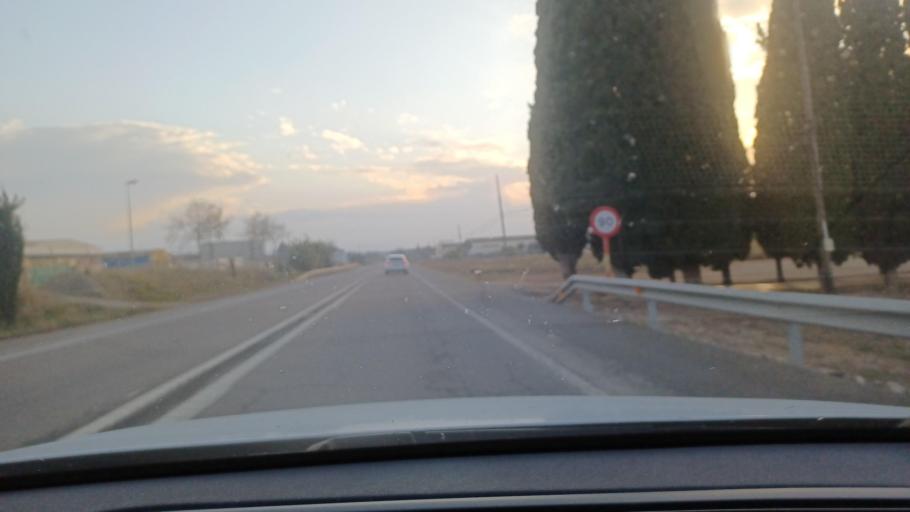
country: ES
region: Catalonia
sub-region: Provincia de Tarragona
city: Camarles
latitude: 40.7759
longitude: 0.6609
